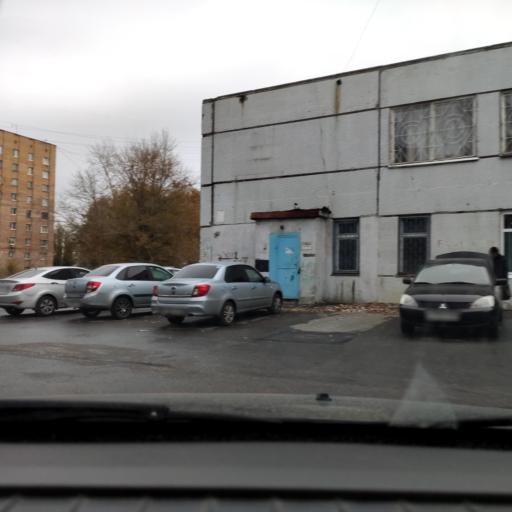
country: RU
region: Samara
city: Tol'yatti
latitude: 53.5098
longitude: 49.4495
